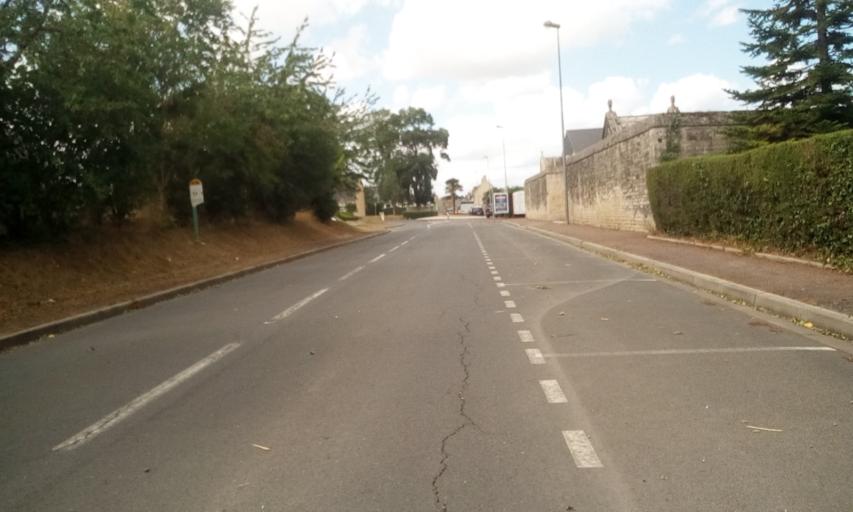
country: FR
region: Lower Normandy
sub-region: Departement du Calvados
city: Creully
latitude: 49.2838
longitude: -0.5331
